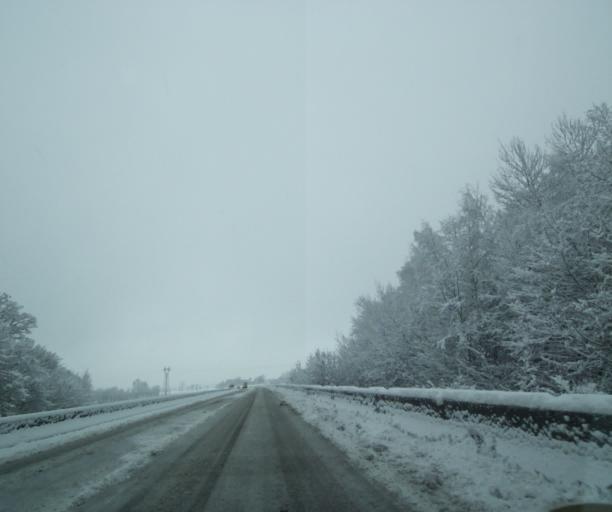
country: FR
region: Champagne-Ardenne
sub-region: Departement de la Haute-Marne
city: Saint-Dizier
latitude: 48.6034
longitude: 4.9046
